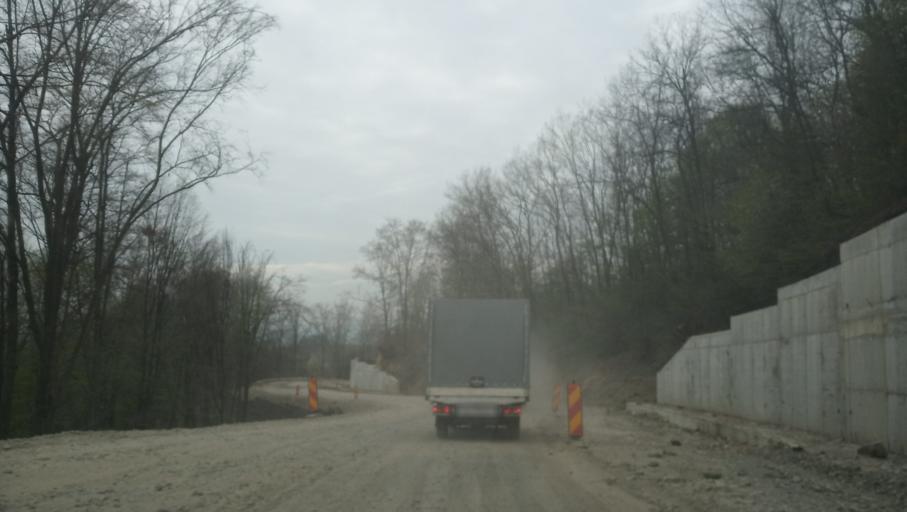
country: RO
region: Arad
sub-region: Comuna Varfurile
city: Varfurile
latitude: 46.3704
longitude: 22.5543
